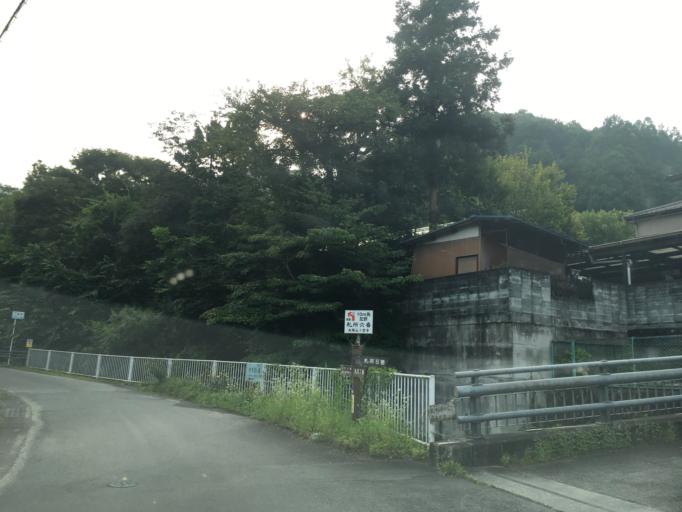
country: JP
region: Saitama
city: Chichibu
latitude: 35.9828
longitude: 139.1137
